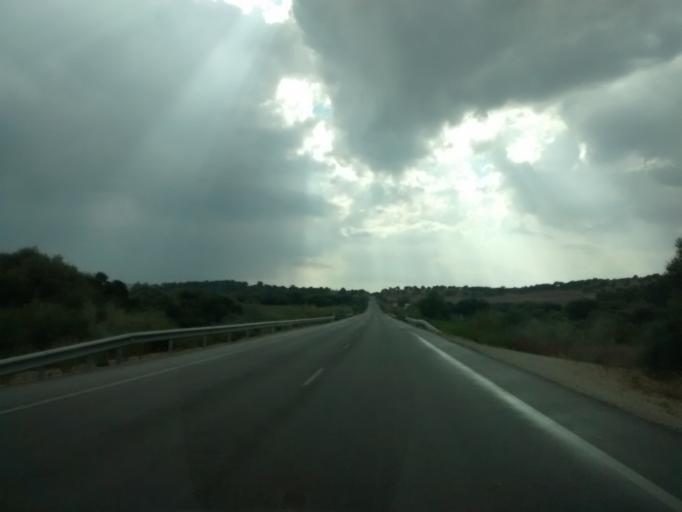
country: ES
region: Andalusia
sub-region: Provincia de Cadiz
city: Prado del Rey
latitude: 36.7461
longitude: -5.6226
